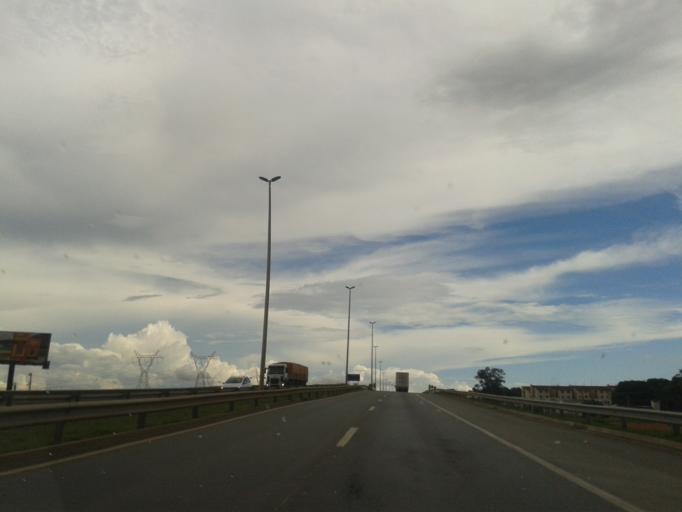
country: BR
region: Goias
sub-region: Aparecida De Goiania
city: Aparecida de Goiania
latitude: -16.8169
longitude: -49.2403
